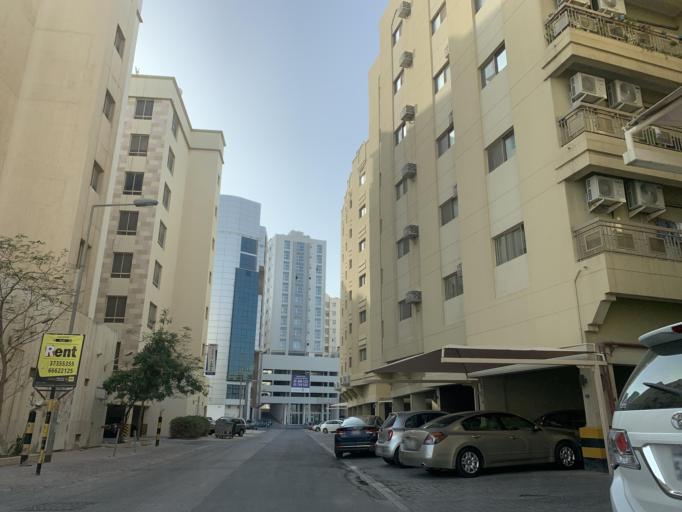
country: BH
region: Manama
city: Manama
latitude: 26.2037
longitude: 50.5824
